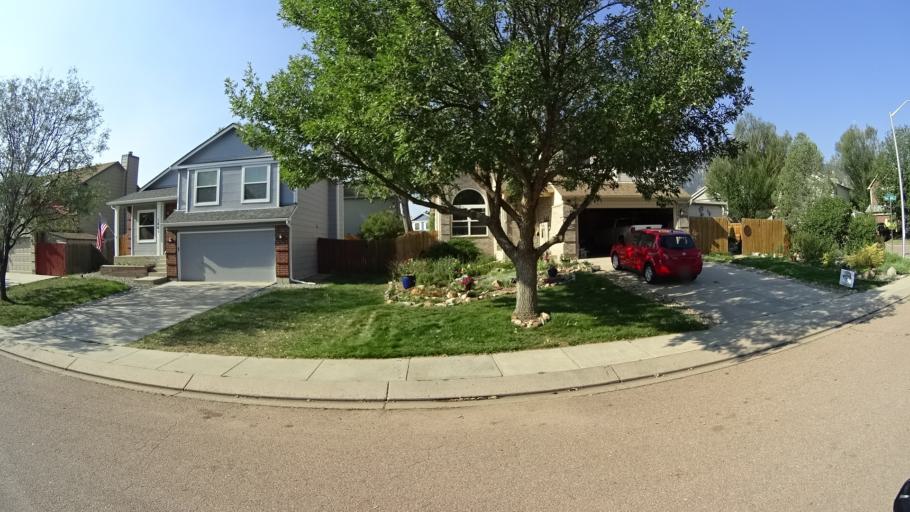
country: US
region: Colorado
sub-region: El Paso County
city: Stratmoor
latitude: 38.7737
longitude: -104.8054
